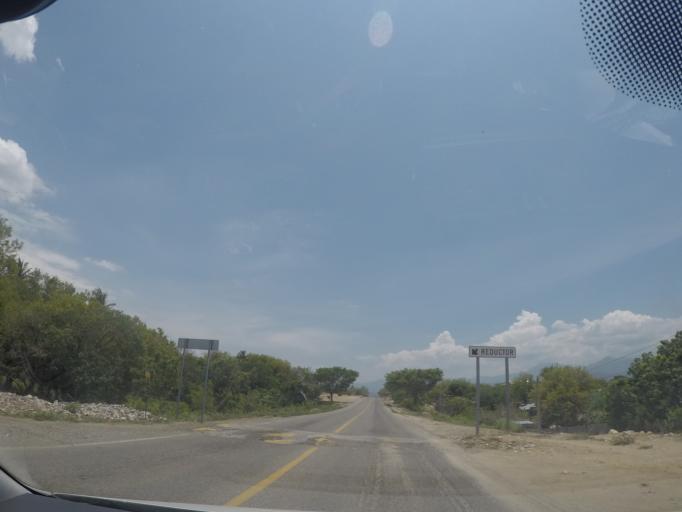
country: MX
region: Oaxaca
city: Santa Maria Jalapa del Marques
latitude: 16.4393
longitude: -95.5082
